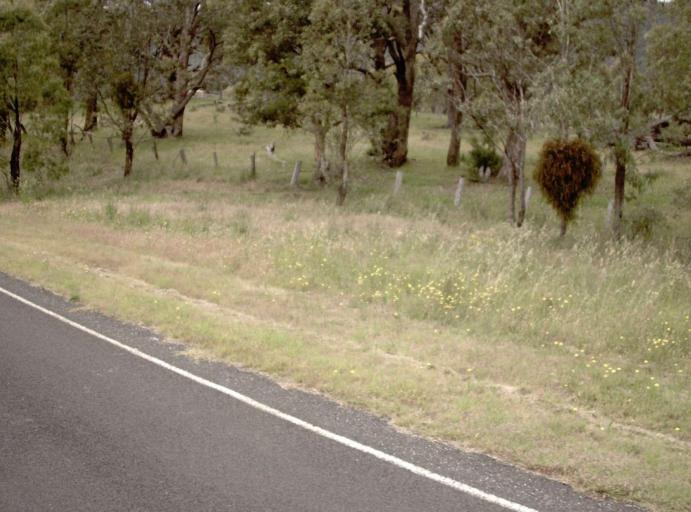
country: AU
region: Victoria
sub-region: East Gippsland
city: Bairnsdale
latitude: -37.5613
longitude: 147.1934
